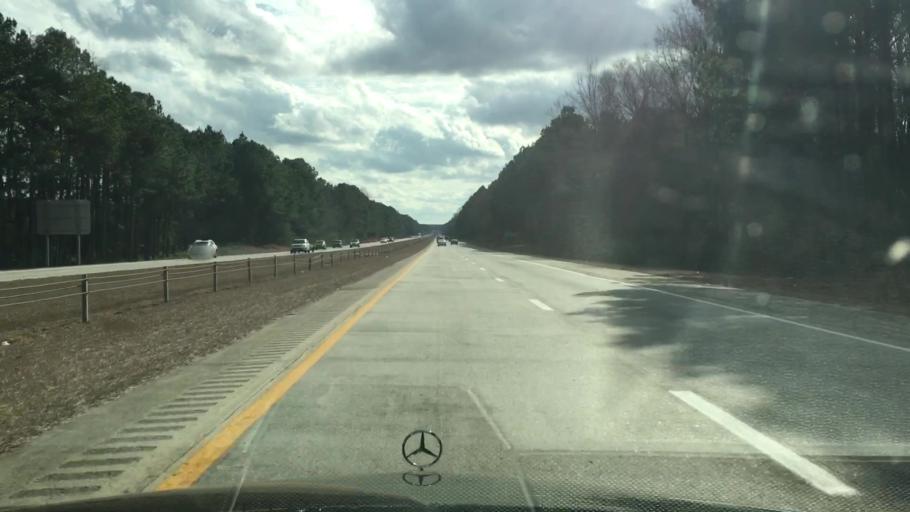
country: US
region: North Carolina
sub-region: Johnston County
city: Benson
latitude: 35.5064
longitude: -78.5552
